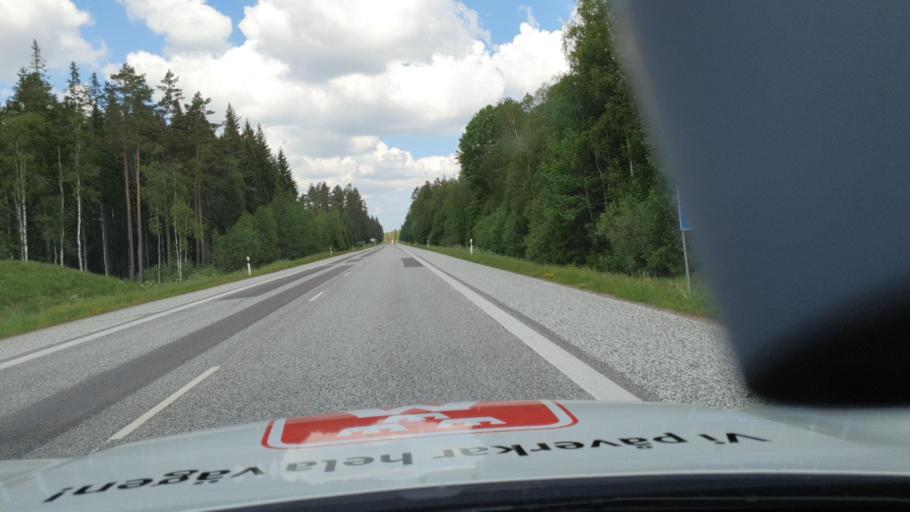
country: SE
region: Joenkoeping
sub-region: Jonkopings Kommun
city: Odensjo
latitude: 57.6256
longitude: 14.2032
